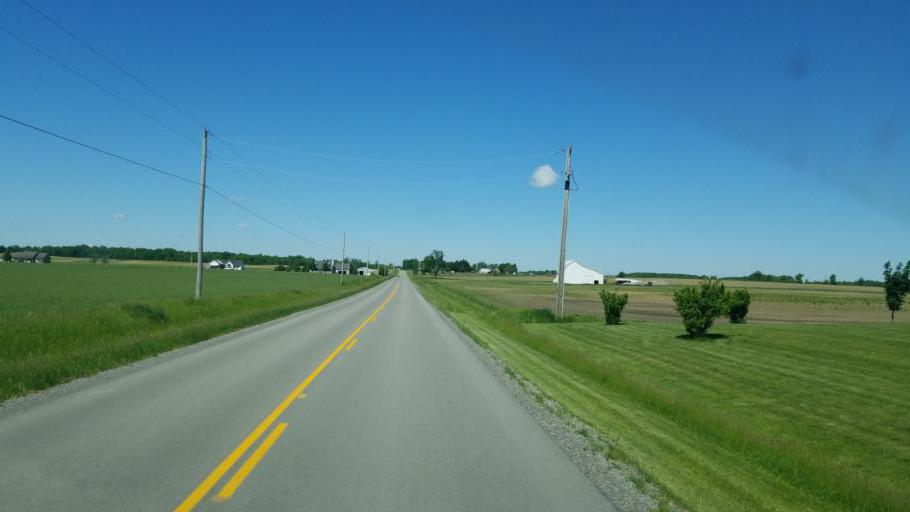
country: US
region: Ohio
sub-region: Logan County
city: Russells Point
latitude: 40.4261
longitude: -83.8349
